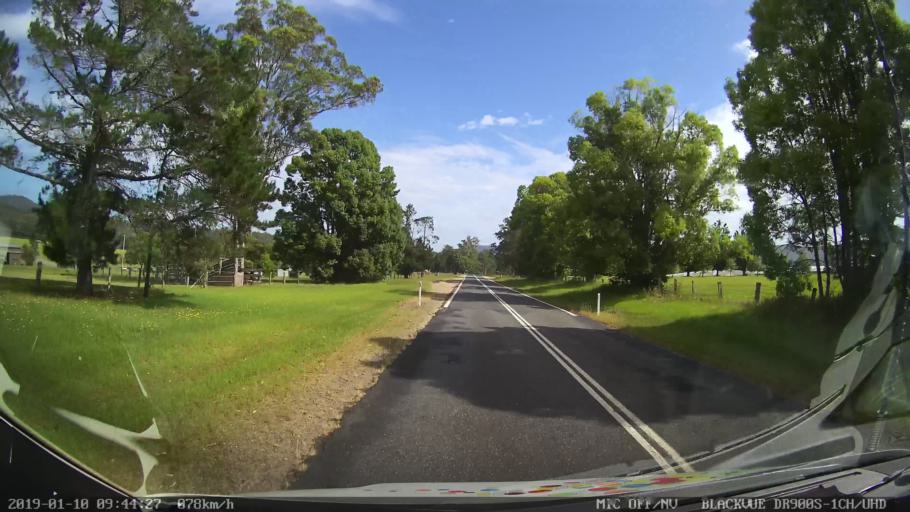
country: AU
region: New South Wales
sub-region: Coffs Harbour
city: Nana Glen
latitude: -30.1166
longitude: 153.0036
